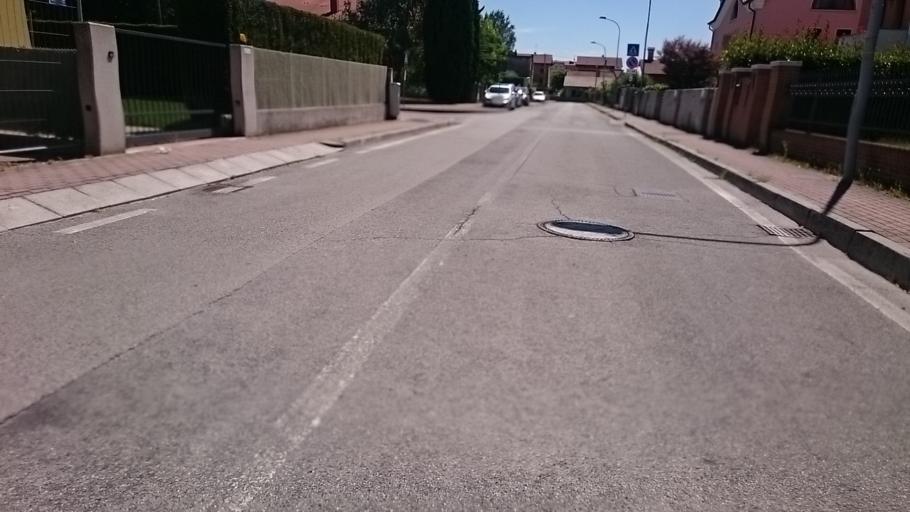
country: IT
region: Veneto
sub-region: Provincia di Venezia
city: Pianiga
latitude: 45.4614
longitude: 11.9919
